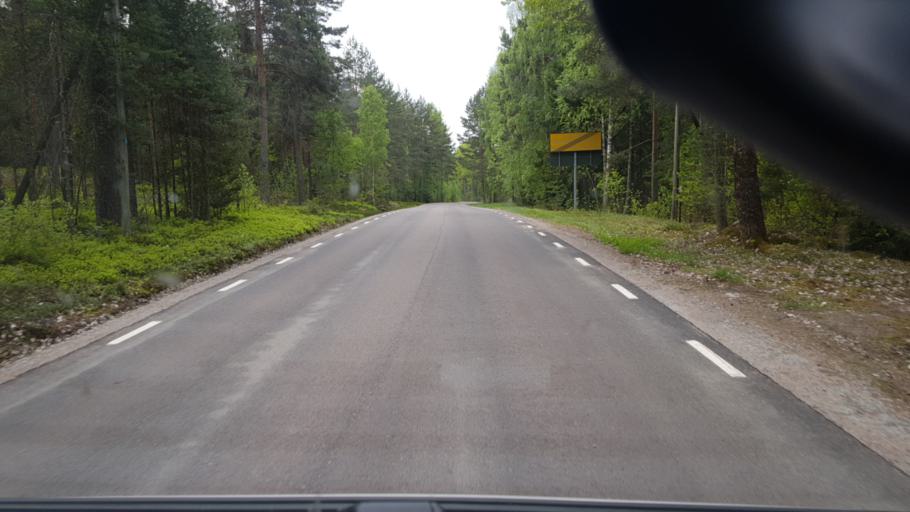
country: SE
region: Vaermland
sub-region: Arvika Kommun
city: Arvika
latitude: 59.5351
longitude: 12.7415
